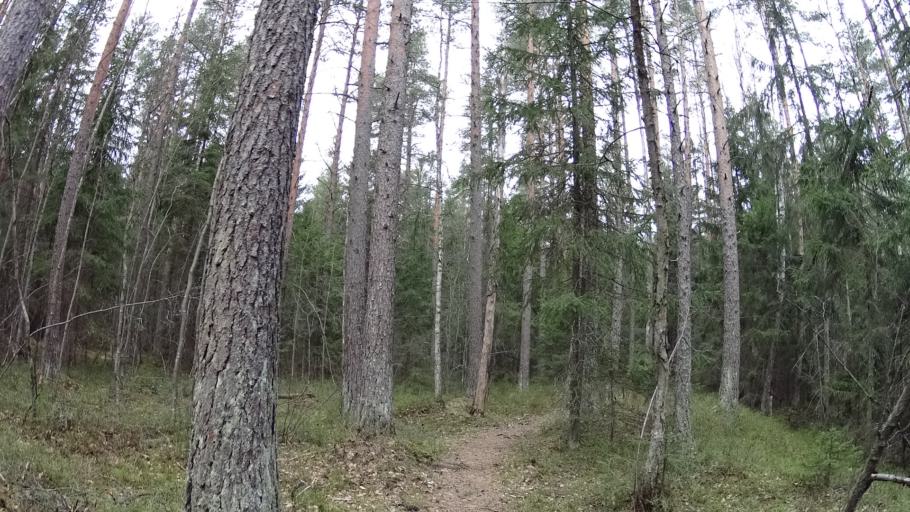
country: FI
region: Uusimaa
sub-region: Helsinki
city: Kilo
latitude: 60.2427
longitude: 24.7874
